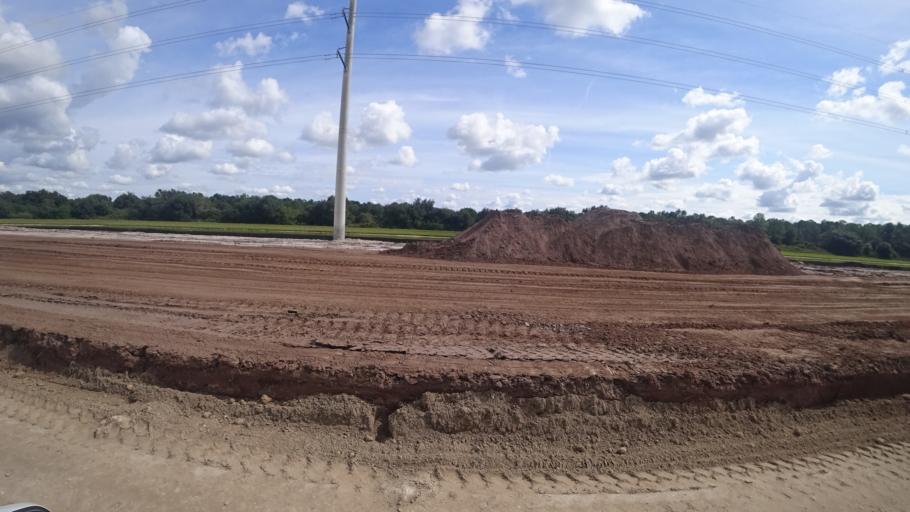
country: US
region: Florida
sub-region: Sarasota County
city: The Meadows
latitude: 27.4296
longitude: -82.3522
